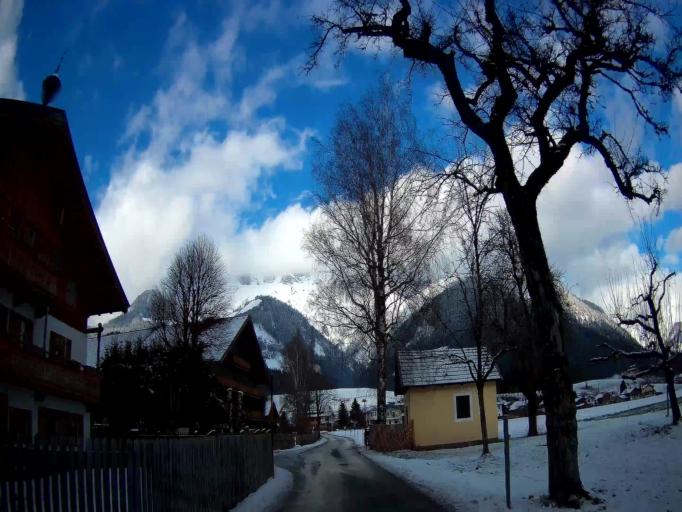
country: AT
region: Salzburg
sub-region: Politischer Bezirk Zell am See
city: Leogang
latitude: 47.4427
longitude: 12.7963
